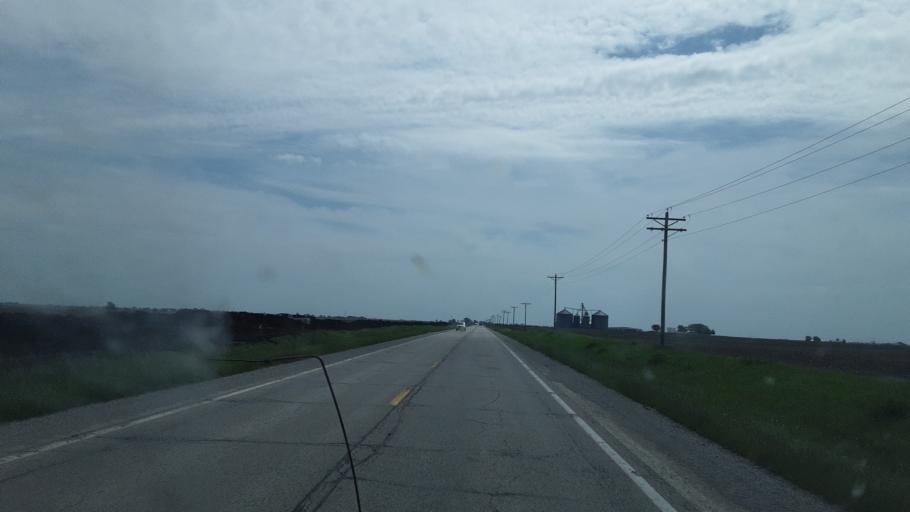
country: US
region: Illinois
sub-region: Logan County
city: Atlanta
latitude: 40.3120
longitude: -89.1456
